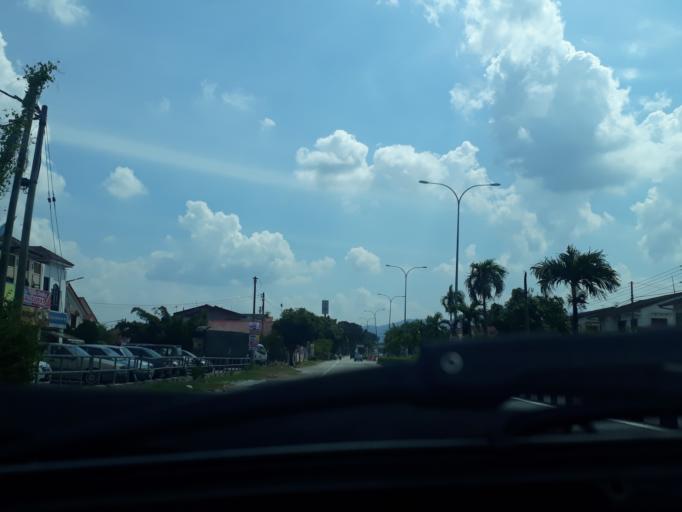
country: MY
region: Perak
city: Ipoh
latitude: 4.5773
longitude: 101.0962
